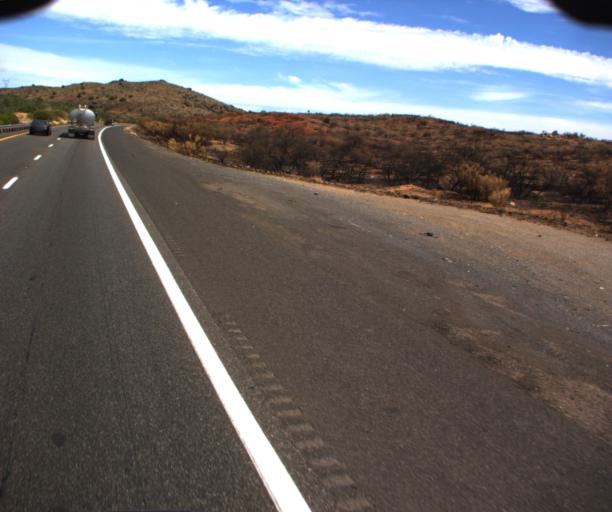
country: US
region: Arizona
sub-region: Yavapai County
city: Cordes Lakes
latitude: 34.2980
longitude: -112.1262
